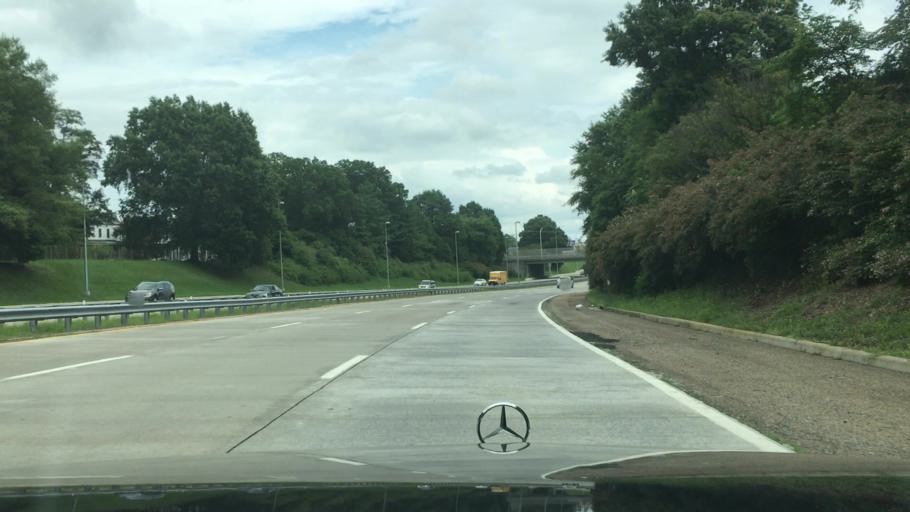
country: US
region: Virginia
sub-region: City of Richmond
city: Richmond
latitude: 37.5477
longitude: -77.4703
